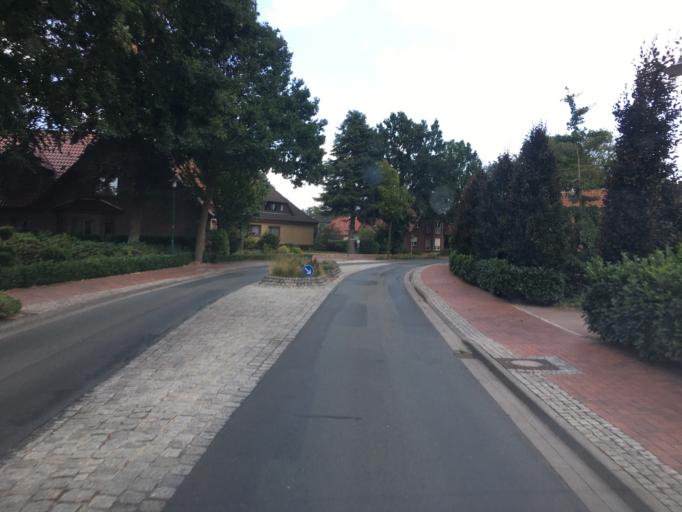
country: DE
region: Lower Saxony
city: Hilkenbrook
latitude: 53.0713
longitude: 7.7025
